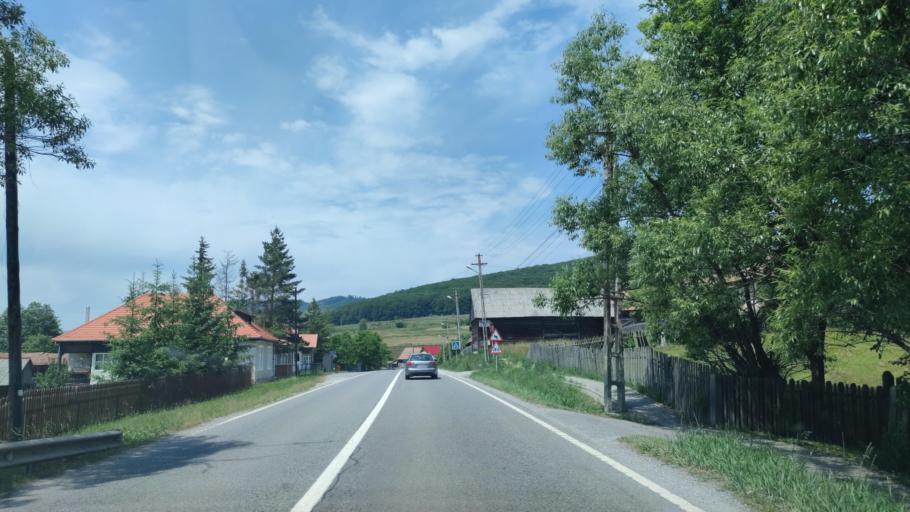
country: RO
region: Harghita
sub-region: Comuna Voslobeni
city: Voslobeni
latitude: 46.6260
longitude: 25.6820
